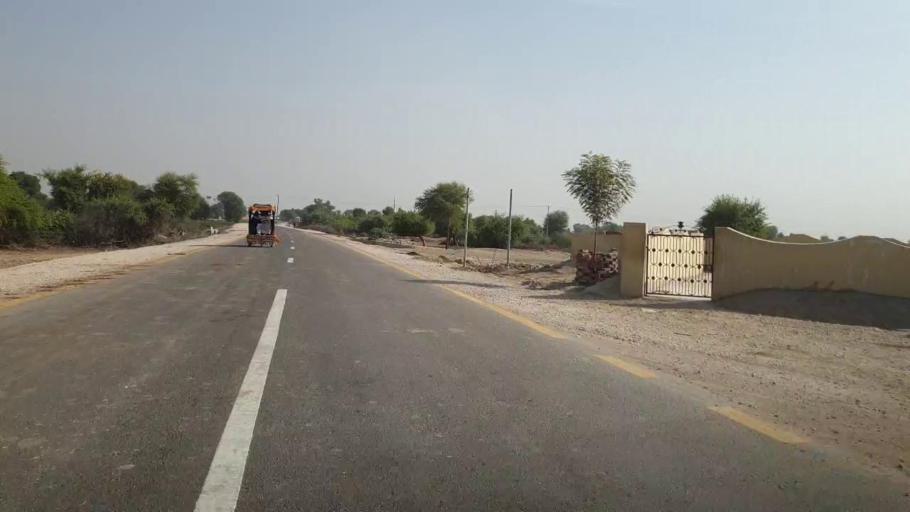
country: PK
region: Sindh
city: Bhan
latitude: 26.5657
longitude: 67.7700
